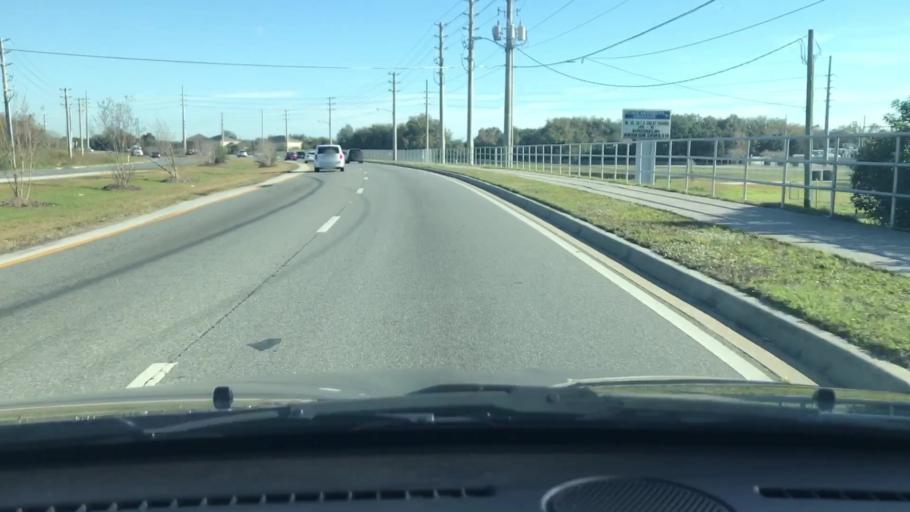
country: US
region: Florida
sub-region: Osceola County
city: Campbell
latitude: 28.2312
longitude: -81.4352
